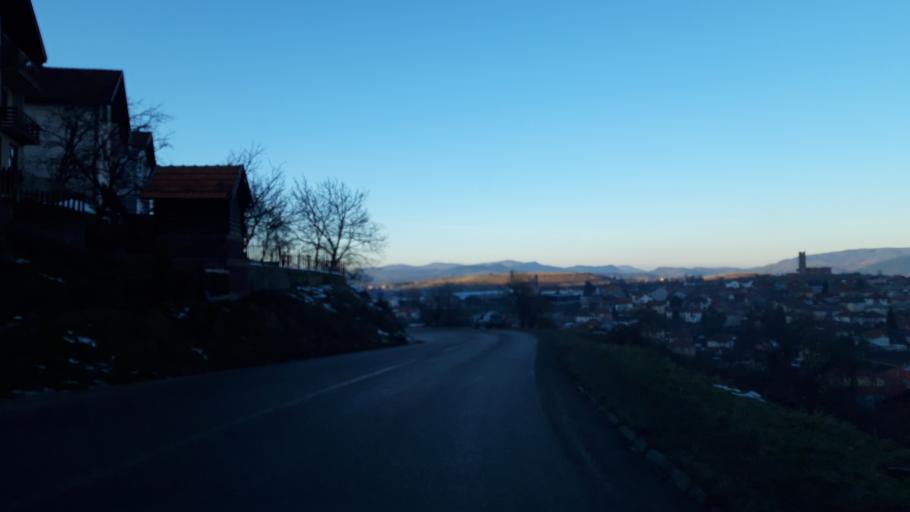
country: BA
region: Republika Srpska
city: Vlasenica
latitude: 44.1795
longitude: 18.9476
